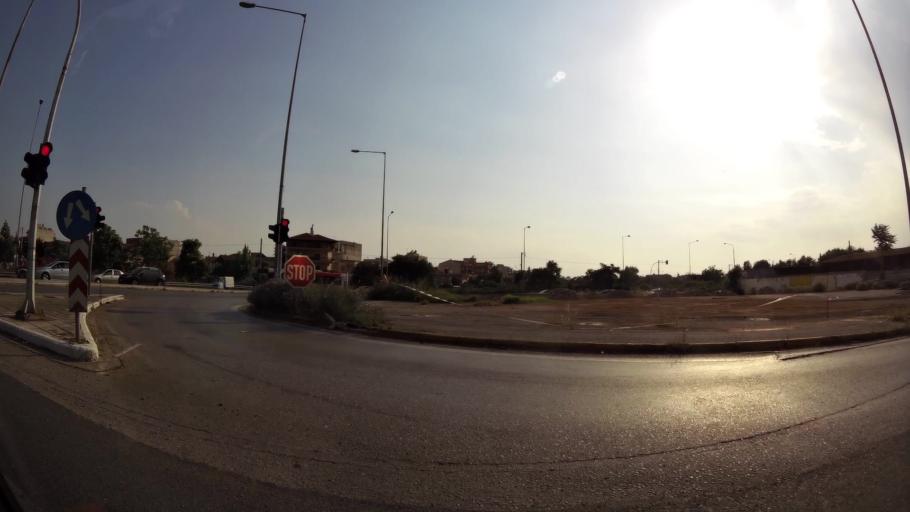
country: GR
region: Central Macedonia
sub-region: Nomos Thessalonikis
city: Nea Magnisia
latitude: 40.6905
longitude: 22.8480
